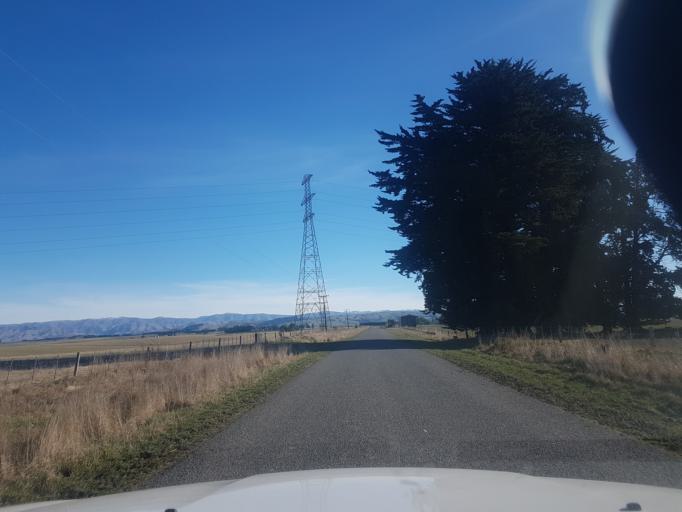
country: NZ
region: Canterbury
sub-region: Timaru District
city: Pleasant Point
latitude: -44.2542
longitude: 171.0383
